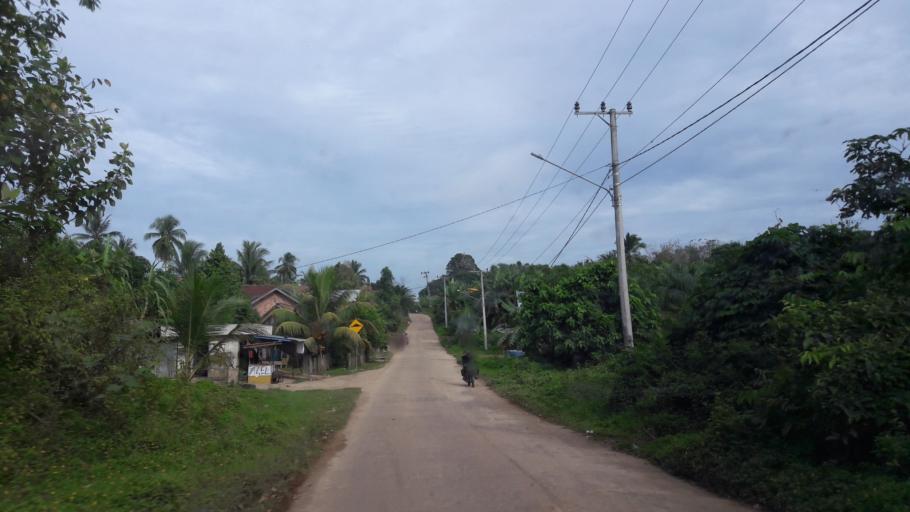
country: ID
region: South Sumatra
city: Gunungmegang Dalam
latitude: -3.2857
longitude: 103.7282
